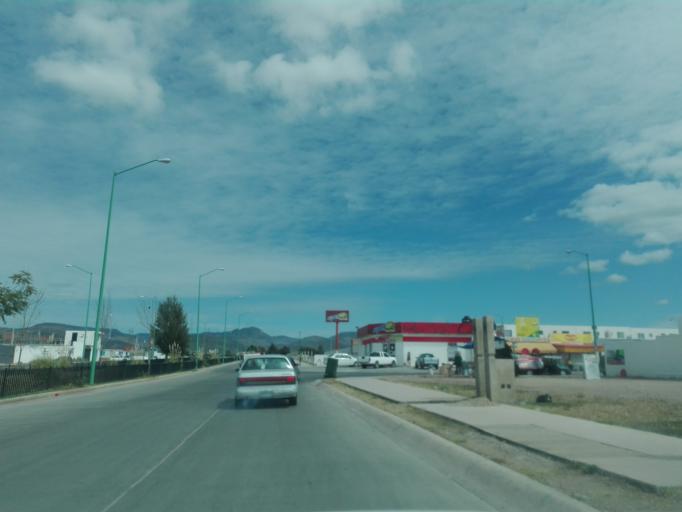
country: MX
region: Guanajuato
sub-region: Leon
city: Ladrilleras del Refugio
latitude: 21.0706
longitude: -101.5646
